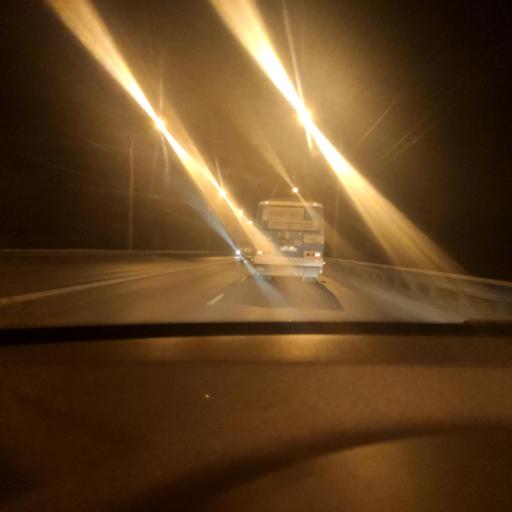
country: RU
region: Samara
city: Samara
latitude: 53.1531
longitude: 50.1891
